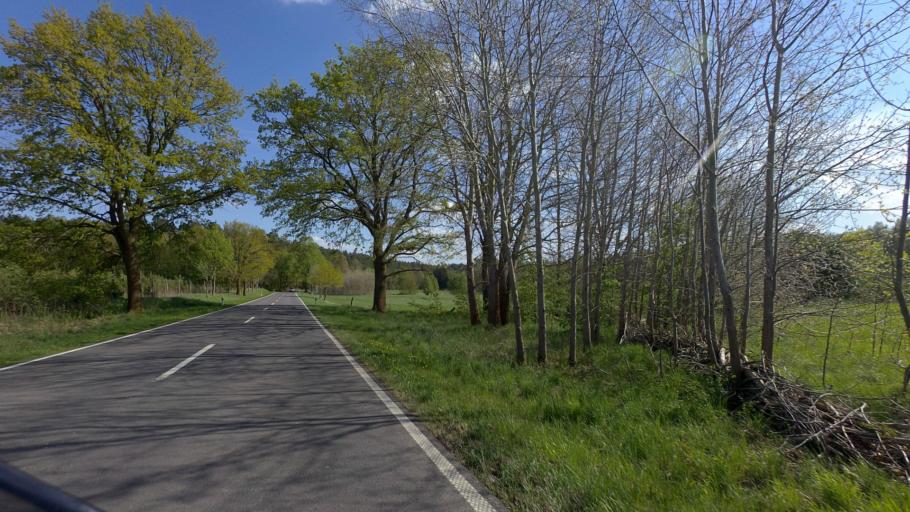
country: DE
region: Brandenburg
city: Templin
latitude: 53.0913
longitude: 13.5042
